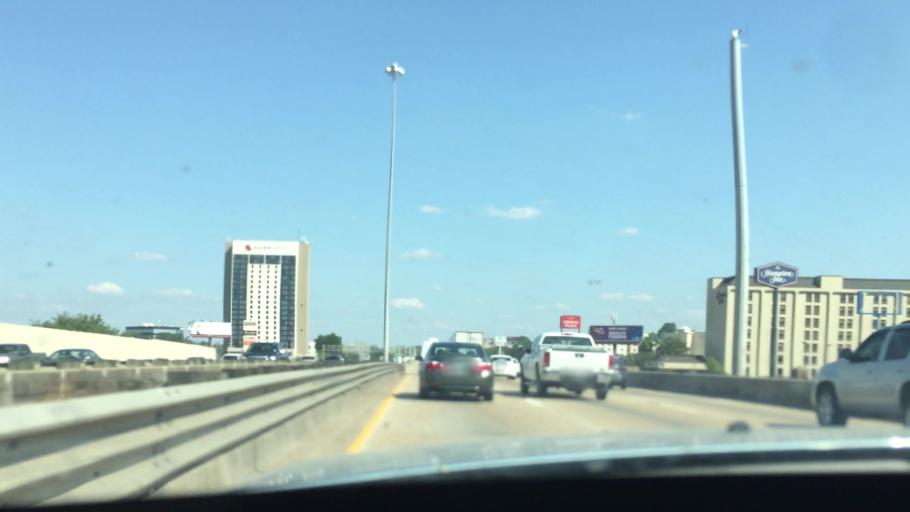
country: US
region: Louisiana
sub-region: East Baton Rouge Parish
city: Baton Rouge
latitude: 30.4229
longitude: -91.1396
